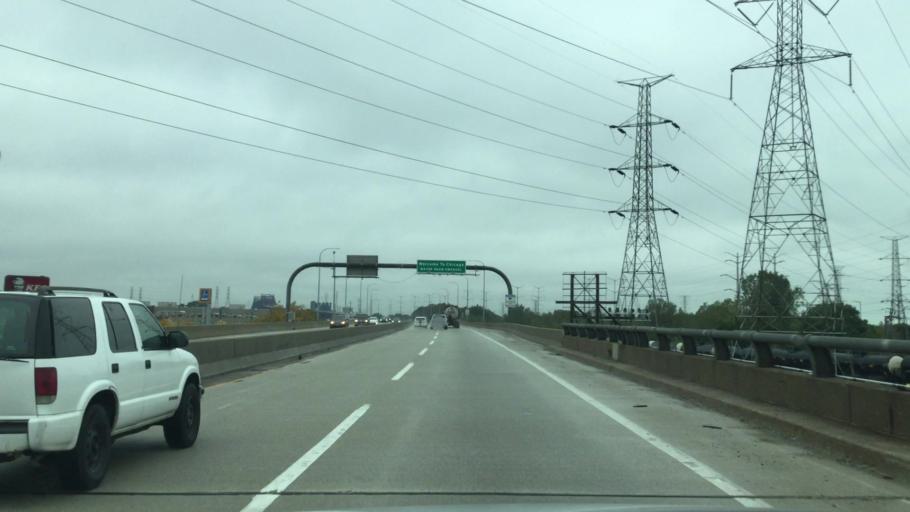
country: US
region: Indiana
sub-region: Lake County
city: Whiting
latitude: 41.7024
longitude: -87.5238
